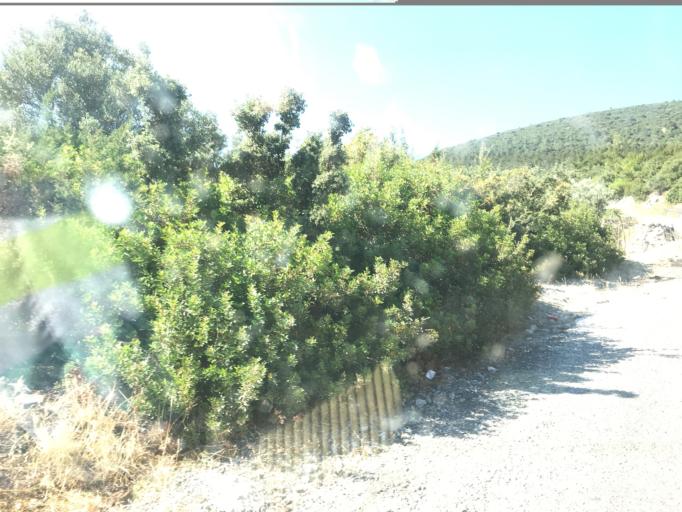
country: TR
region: Mugla
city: Kiulukioi
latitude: 37.3724
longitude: 27.4895
